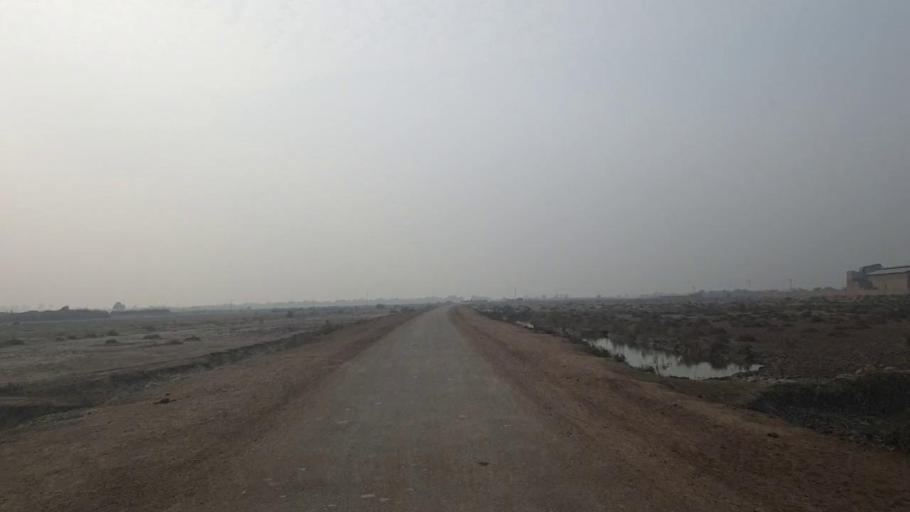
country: PK
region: Sindh
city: Tando Adam
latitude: 25.8230
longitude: 68.6848
